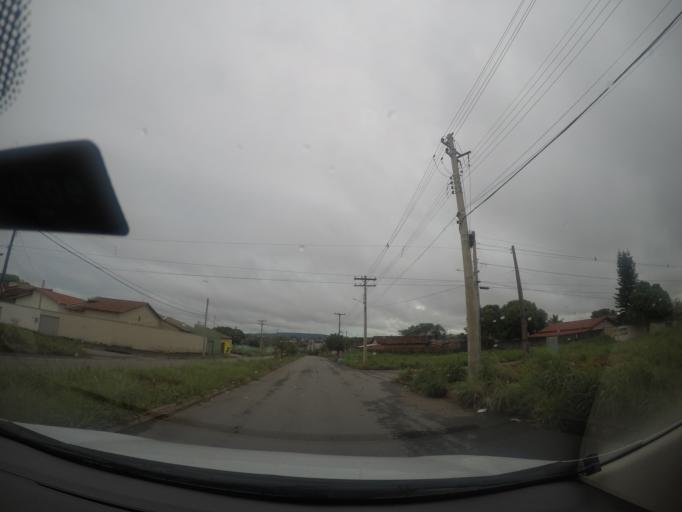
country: BR
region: Goias
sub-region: Aparecida De Goiania
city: Aparecida de Goiania
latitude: -16.7562
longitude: -49.3178
